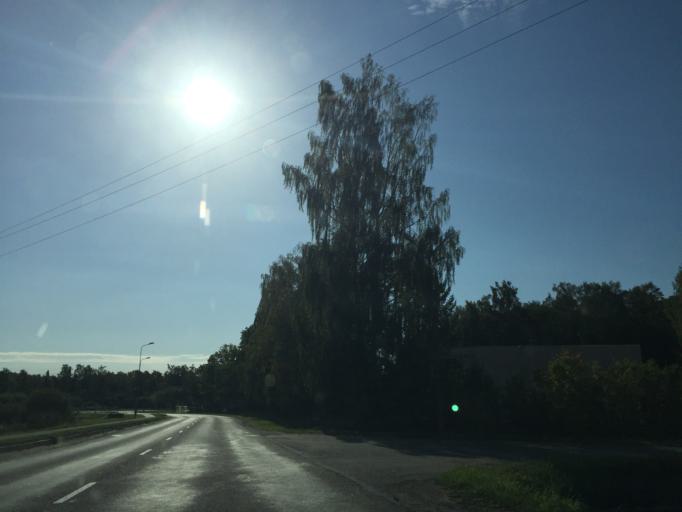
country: LV
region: Limbazu Rajons
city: Limbazi
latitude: 57.5106
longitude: 24.6950
